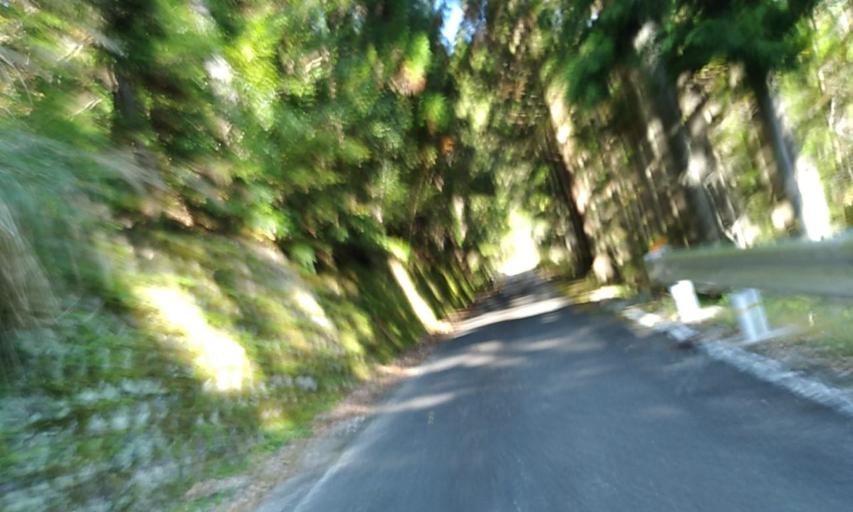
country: JP
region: Wakayama
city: Shingu
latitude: 33.9106
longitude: 135.9879
